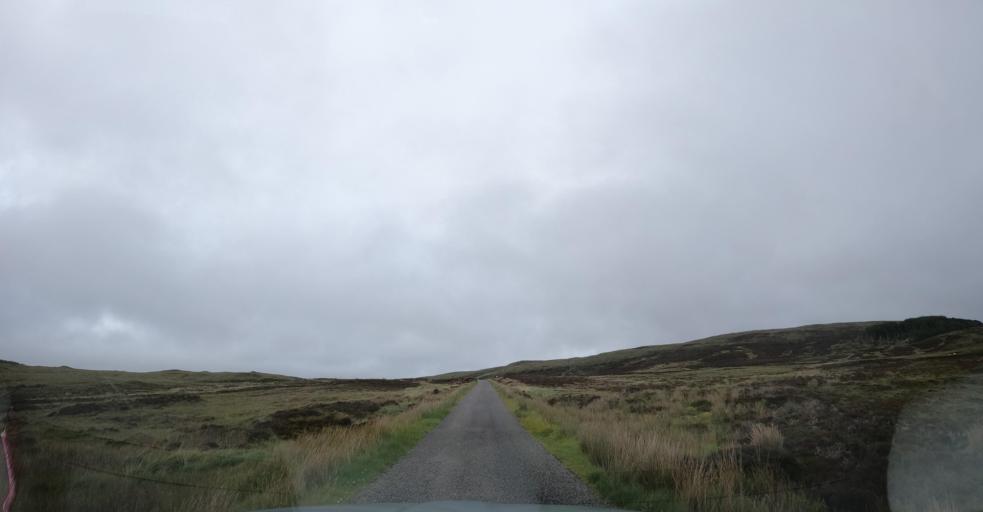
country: GB
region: Scotland
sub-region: Eilean Siar
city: Isle of North Uist
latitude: 57.6078
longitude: -7.3762
